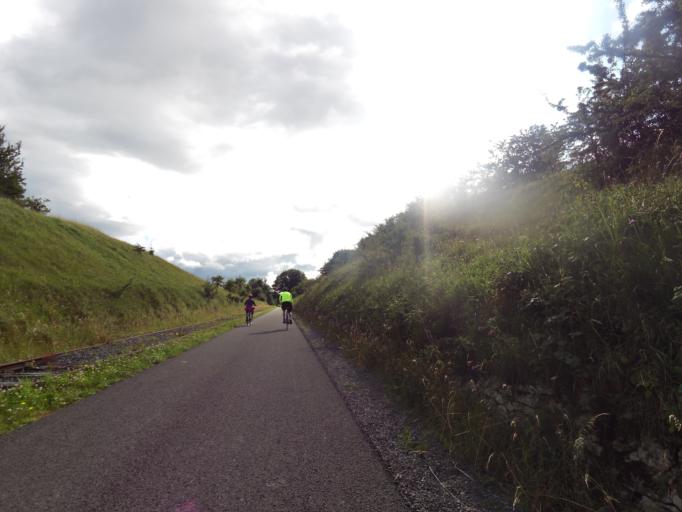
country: IE
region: Leinster
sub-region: An Iarmhi
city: Kilbeggan
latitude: 53.4680
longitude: -7.4972
